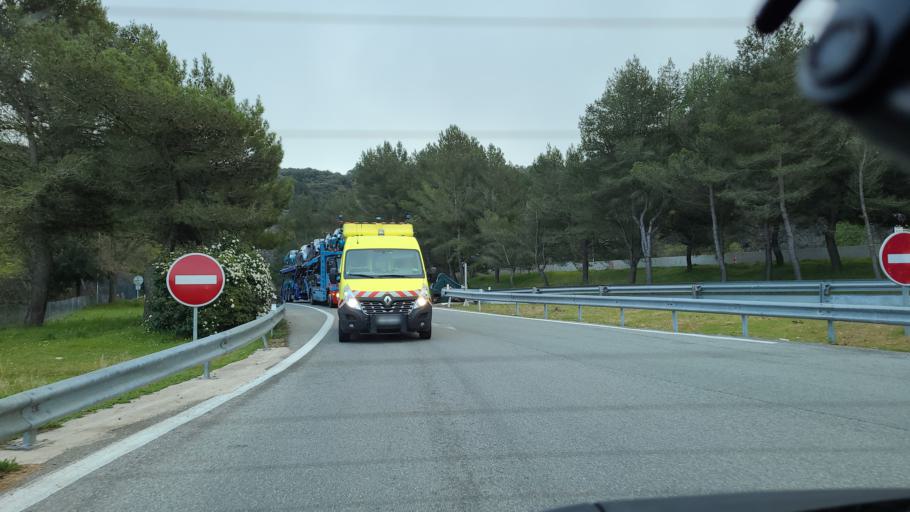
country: FR
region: Provence-Alpes-Cote d'Azur
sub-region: Departement des Alpes-Maritimes
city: La Turbie
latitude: 43.7544
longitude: 7.3984
